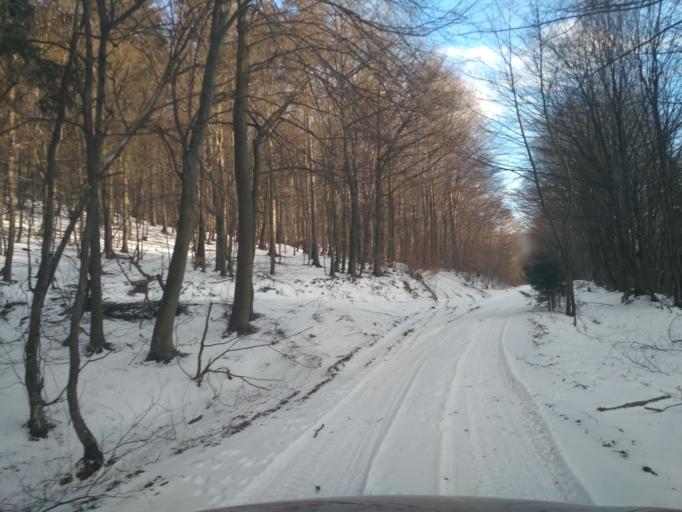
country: SK
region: Kosicky
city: Kosice
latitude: 48.7478
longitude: 21.1512
